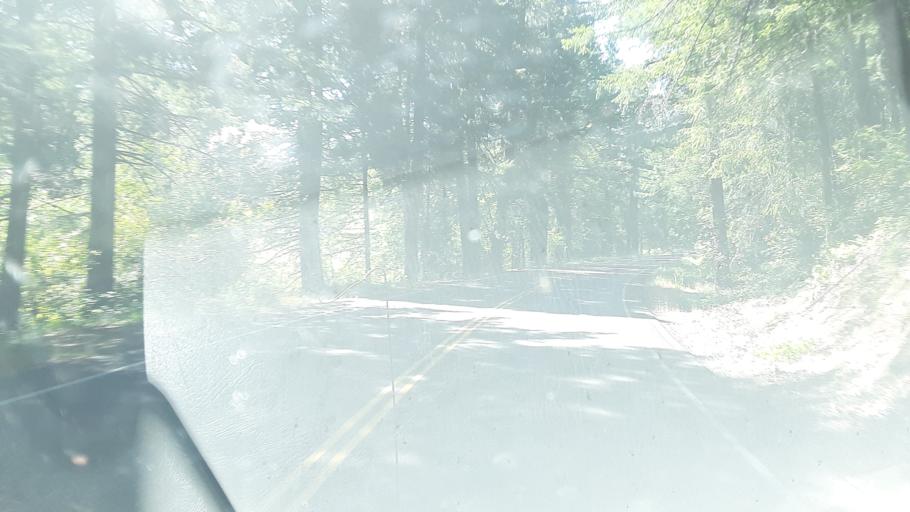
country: US
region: Oregon
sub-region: Josephine County
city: Cave Junction
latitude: 41.9910
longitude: -123.7180
